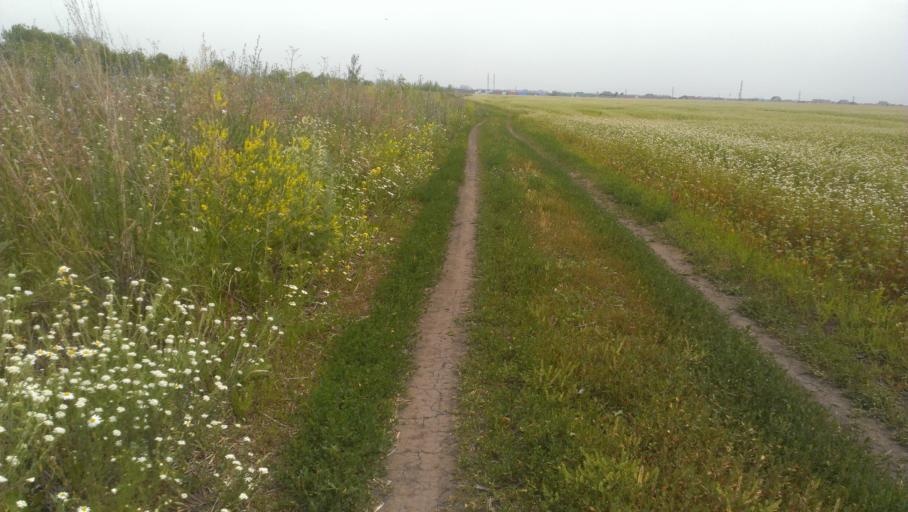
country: RU
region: Altai Krai
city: Novosilikatnyy
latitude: 53.3778
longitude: 83.6380
